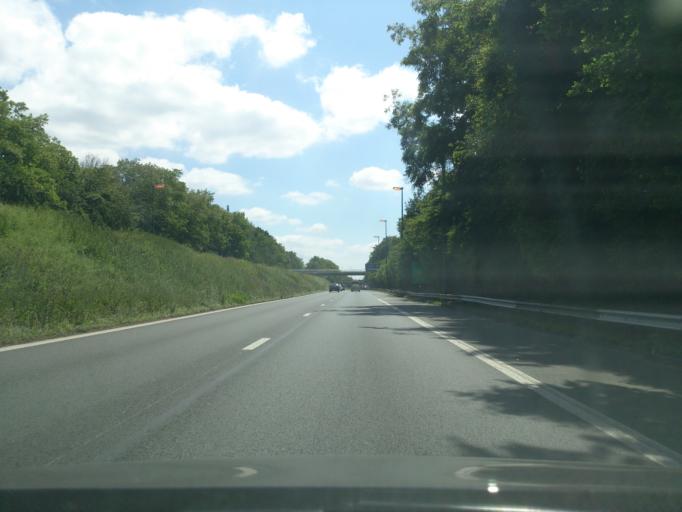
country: BE
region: Wallonia
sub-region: Province du Brabant Wallon
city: Waterloo
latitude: 50.6975
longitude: 4.4128
